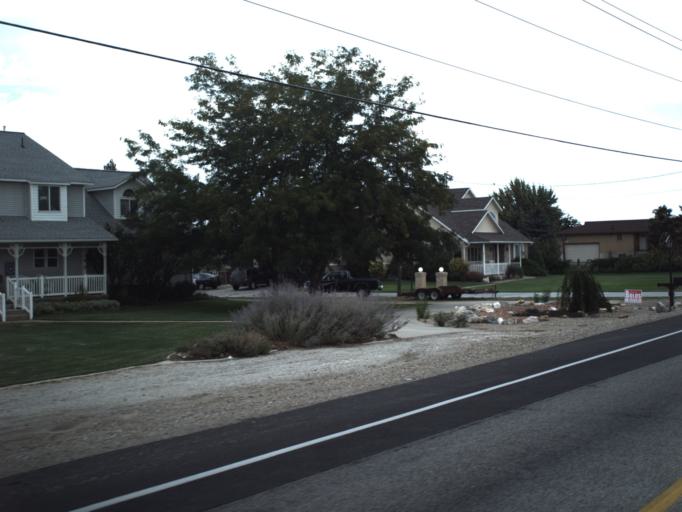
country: US
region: Utah
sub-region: Weber County
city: West Haven
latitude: 41.1991
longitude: -112.0932
